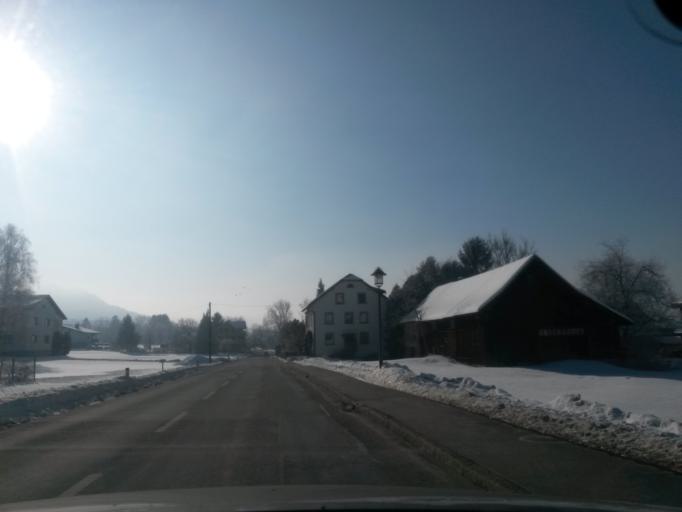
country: AT
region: Vorarlberg
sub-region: Politischer Bezirk Bregenz
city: Hohenweiler
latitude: 47.5870
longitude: 9.7806
